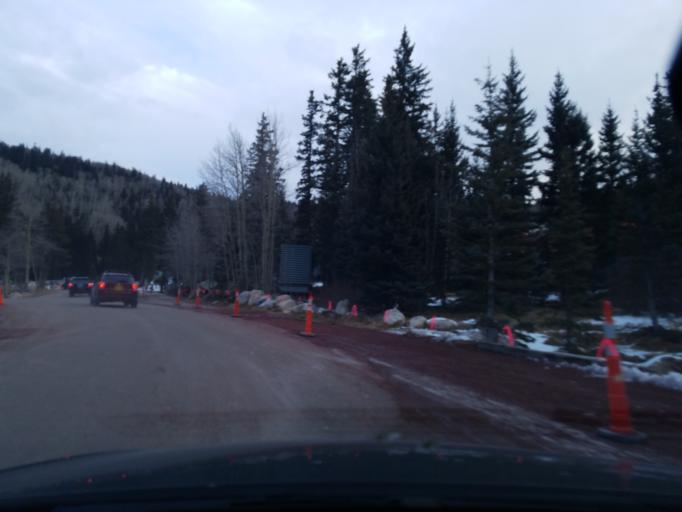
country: US
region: New Mexico
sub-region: Santa Fe County
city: Santa Fe
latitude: 35.7954
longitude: -105.8021
